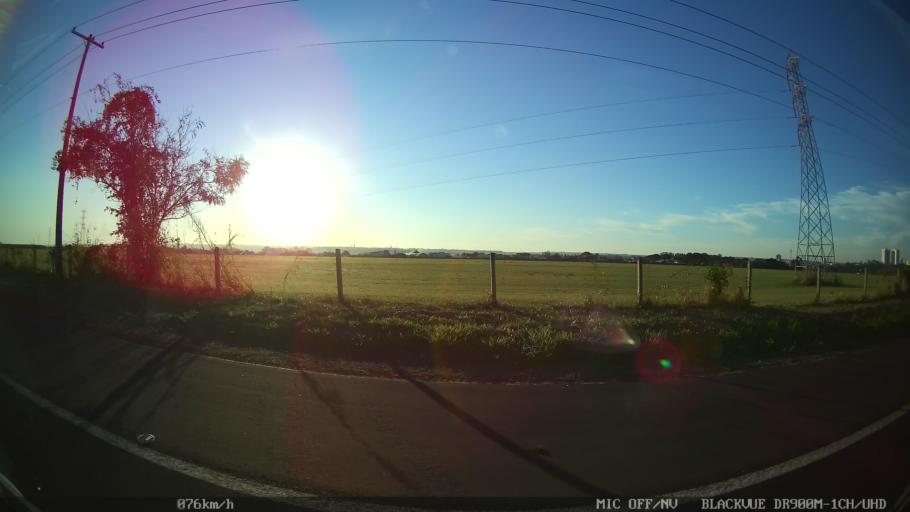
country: BR
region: Sao Paulo
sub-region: Araraquara
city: Araraquara
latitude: -21.8107
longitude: -48.1985
